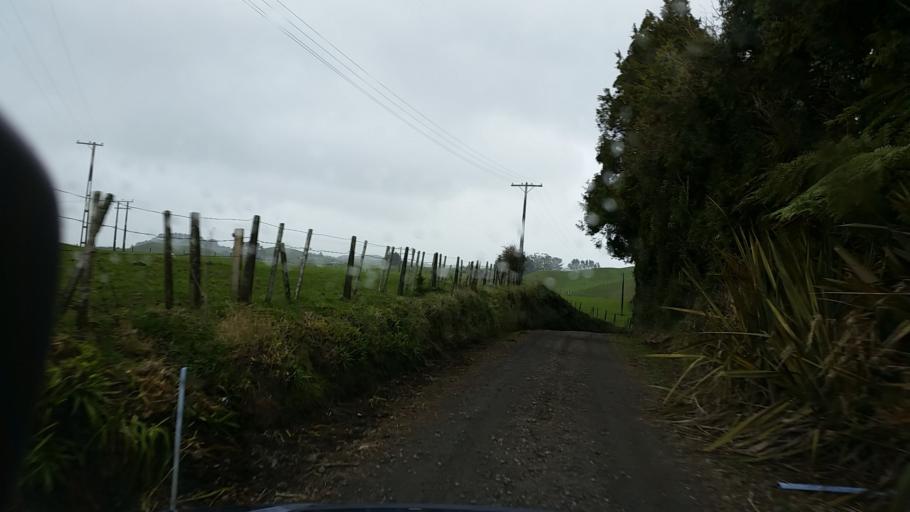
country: NZ
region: Taranaki
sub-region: South Taranaki District
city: Eltham
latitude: -39.2762
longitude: 174.3394
